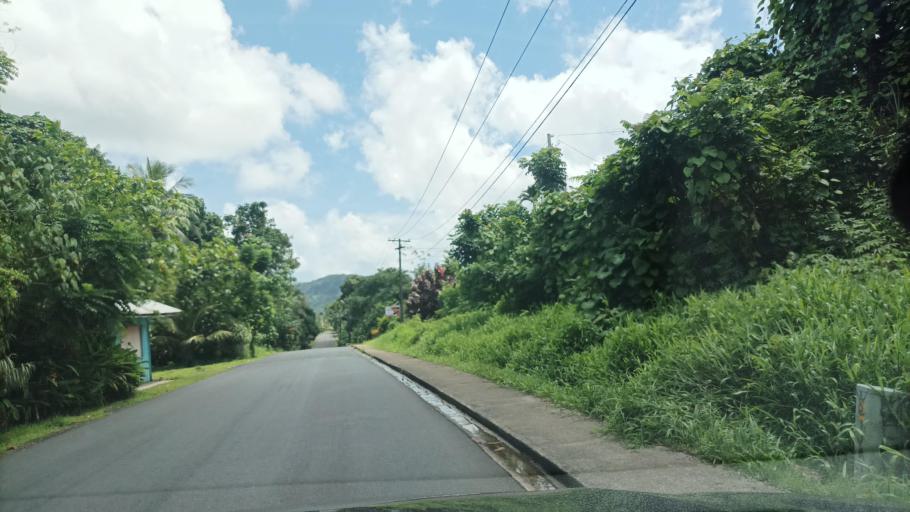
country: FM
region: Pohnpei
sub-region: Sokehs Municipality
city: Palikir - National Government Center
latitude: 6.9307
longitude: 158.1801
